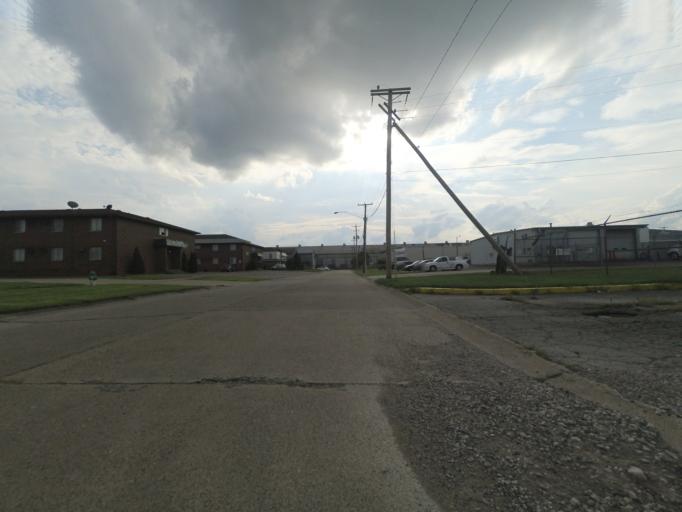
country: US
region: West Virginia
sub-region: Cabell County
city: Huntington
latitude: 38.4296
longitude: -82.4152
